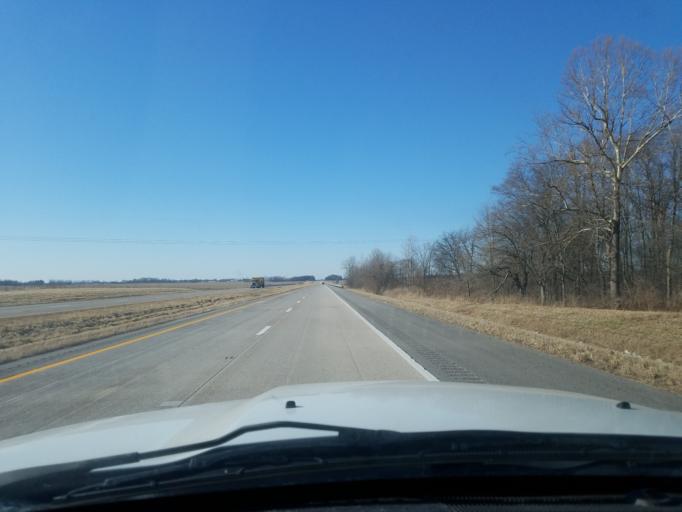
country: US
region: Kentucky
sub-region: Henderson County
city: Henderson
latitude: 37.7988
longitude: -87.5093
